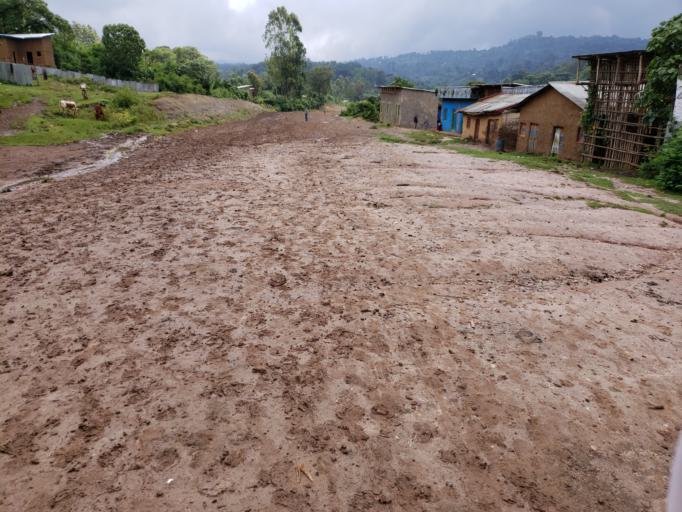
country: ET
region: Oromiya
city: Dodola
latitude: 6.4937
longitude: 39.4418
